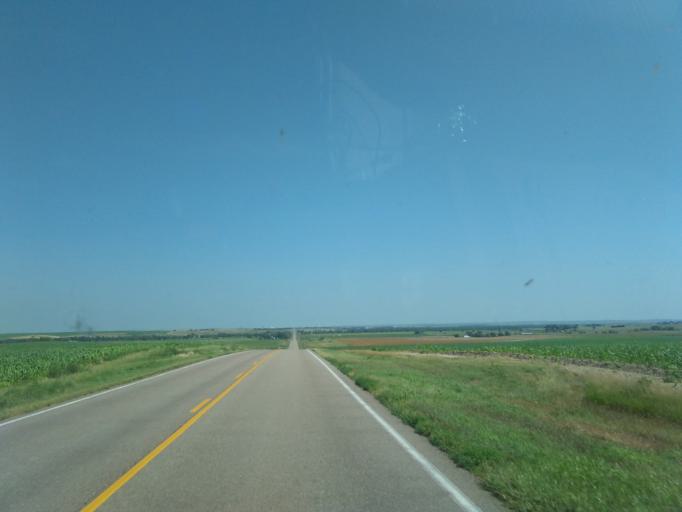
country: US
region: Nebraska
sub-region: Dundy County
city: Benkelman
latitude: 39.9840
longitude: -101.5419
